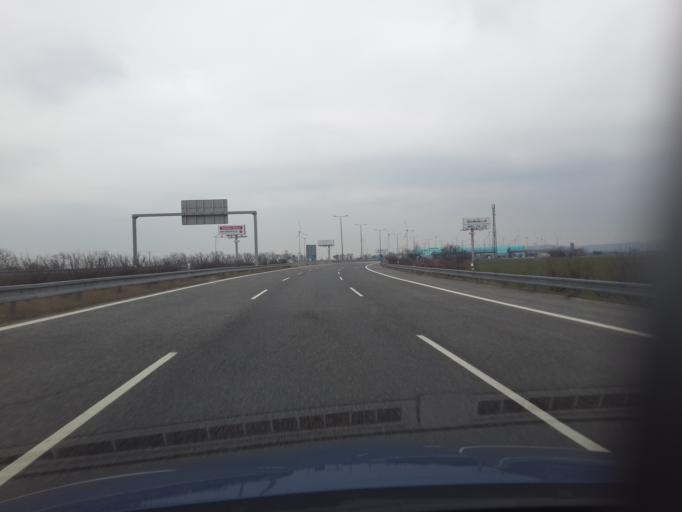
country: AT
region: Burgenland
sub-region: Politischer Bezirk Neusiedl am See
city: Kittsee
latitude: 48.0690
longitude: 17.0843
